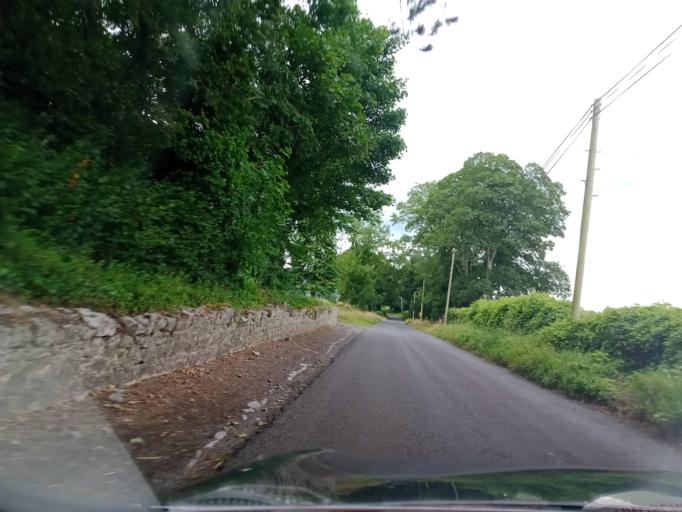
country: IE
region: Leinster
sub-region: Laois
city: Stradbally
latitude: 52.9893
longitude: -7.1749
